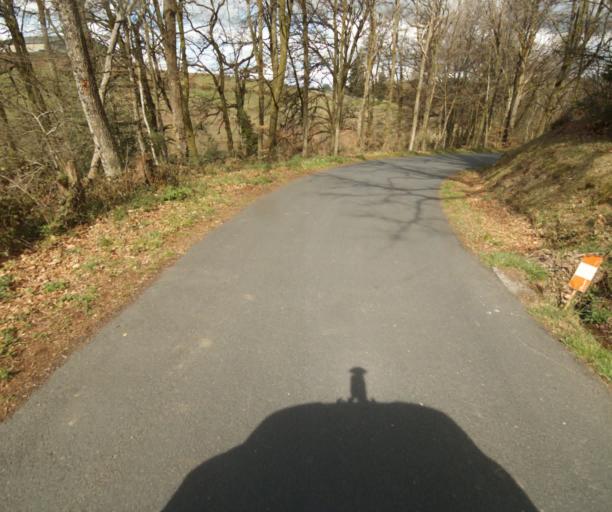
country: FR
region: Limousin
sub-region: Departement de la Correze
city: Correze
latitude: 45.3688
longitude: 1.8881
